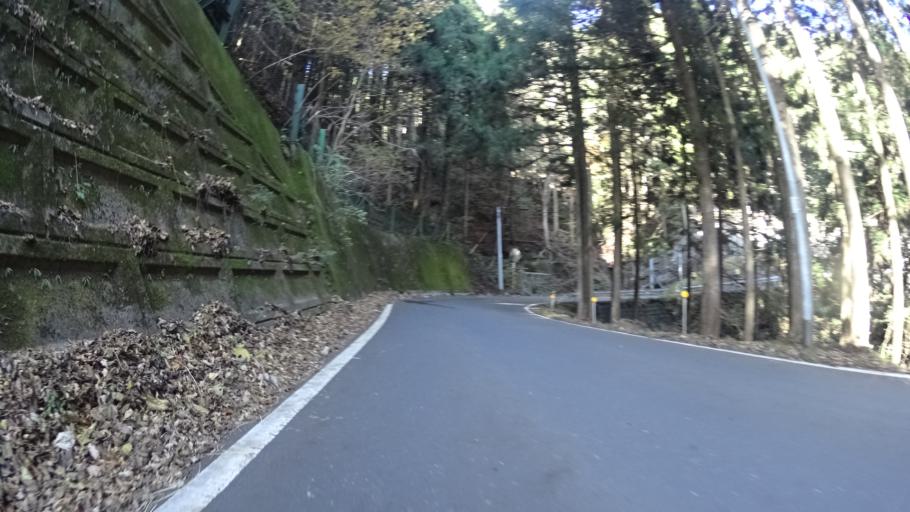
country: JP
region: Saitama
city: Chichibu
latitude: 35.9292
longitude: 139.1512
